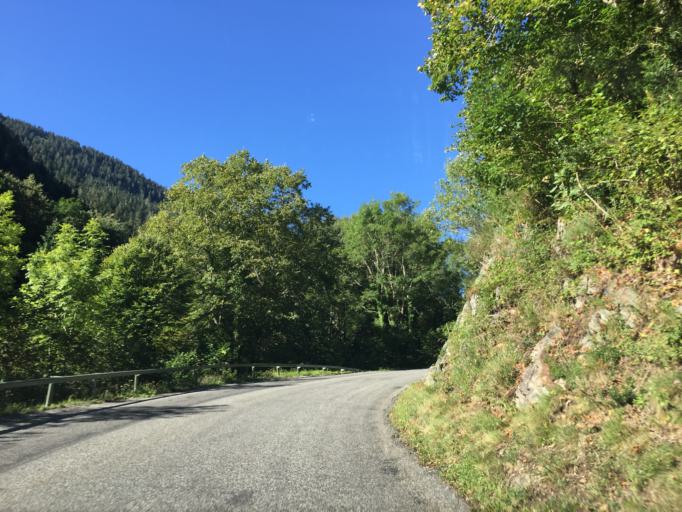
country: FR
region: Midi-Pyrenees
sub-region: Departement des Hautes-Pyrenees
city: Saint-Lary-Soulan
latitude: 42.8565
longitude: 0.3170
